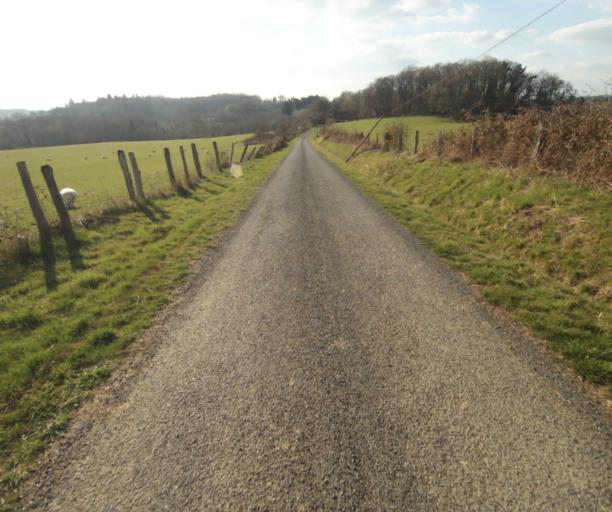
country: FR
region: Limousin
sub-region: Departement de la Correze
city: Saint-Clement
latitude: 45.3446
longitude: 1.6509
